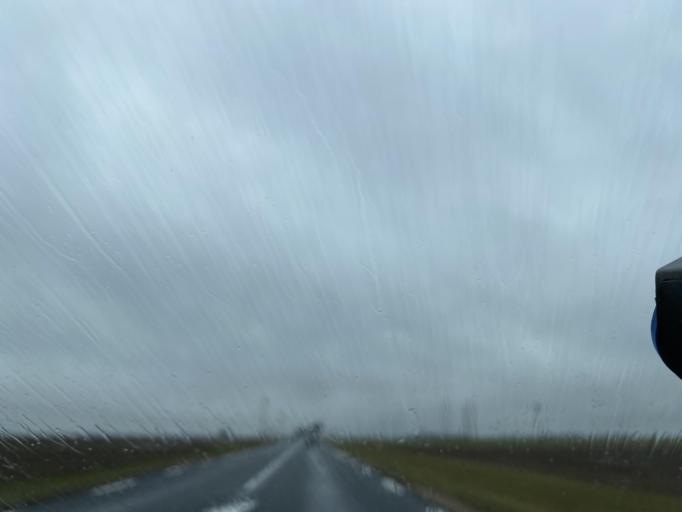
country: FR
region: Centre
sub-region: Departement d'Eure-et-Loir
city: Janville
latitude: 48.1832
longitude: 1.8323
